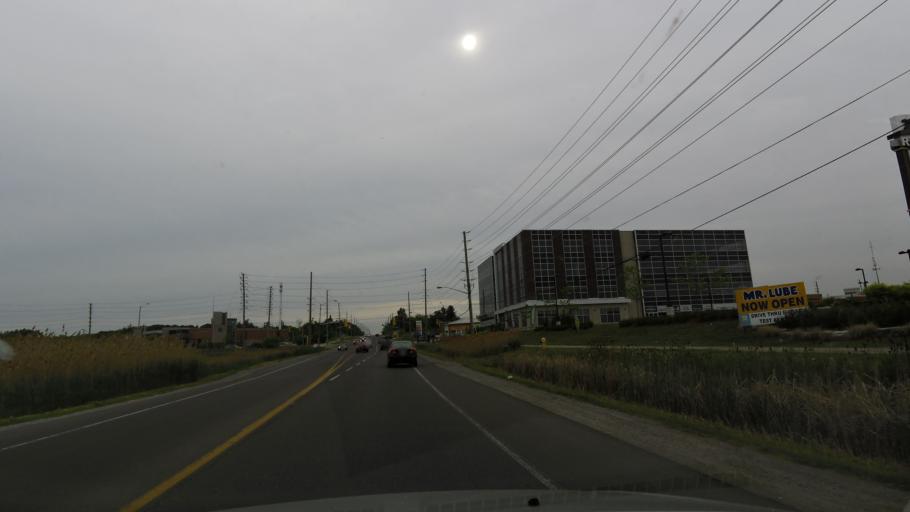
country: CA
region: Ontario
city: Ajax
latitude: 43.8821
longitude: -79.0170
